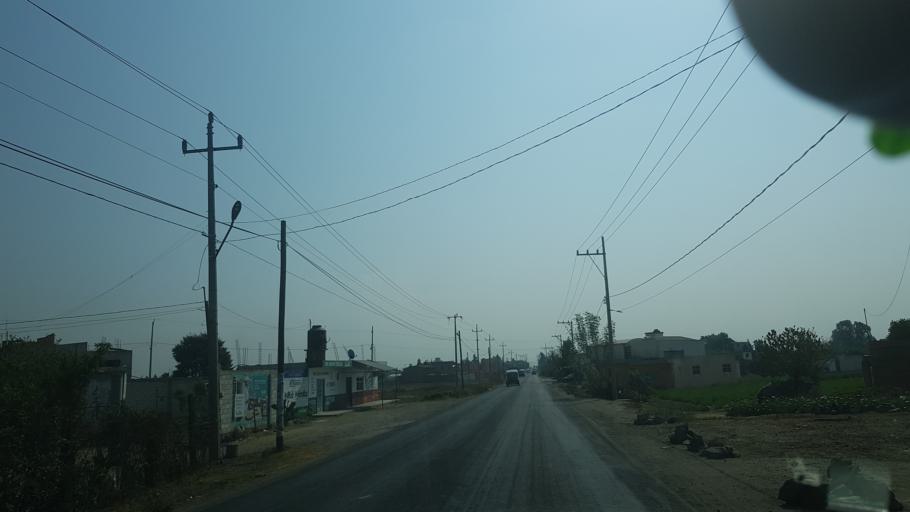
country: MX
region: Puebla
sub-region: San Jeronimo Tecuanipan
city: Los Reyes Tlanechicolpan
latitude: 19.0530
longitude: -98.3423
